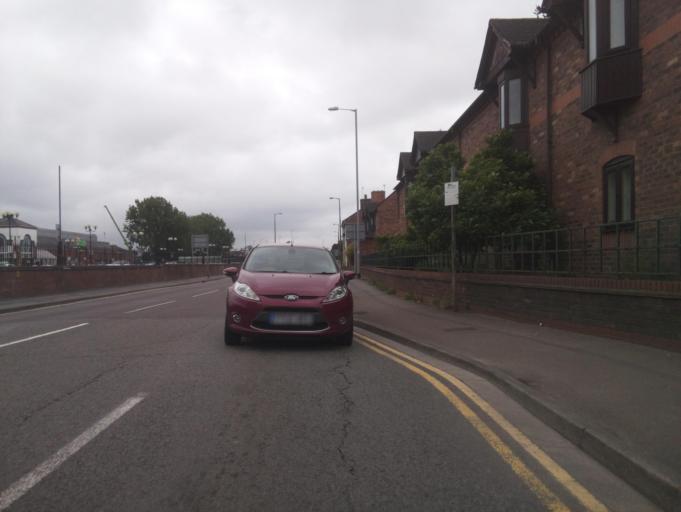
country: GB
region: England
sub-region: Staffordshire
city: Burton upon Trent
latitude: 52.8015
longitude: -1.6360
